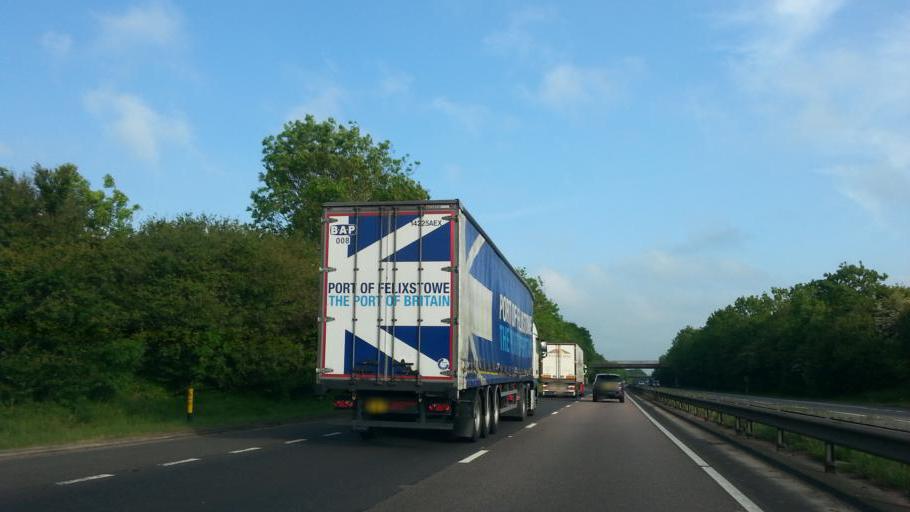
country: GB
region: England
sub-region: Nottinghamshire
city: Tuxford
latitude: 53.2035
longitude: -0.8612
